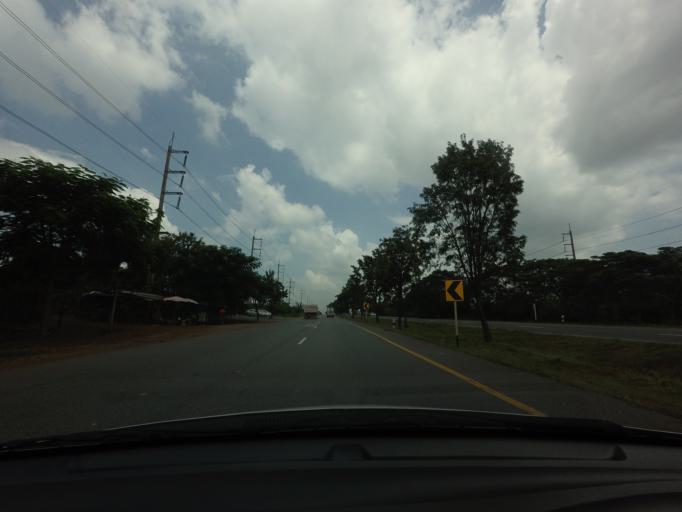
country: TH
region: Prachin Buri
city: Kabin Buri
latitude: 13.9071
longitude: 101.6637
